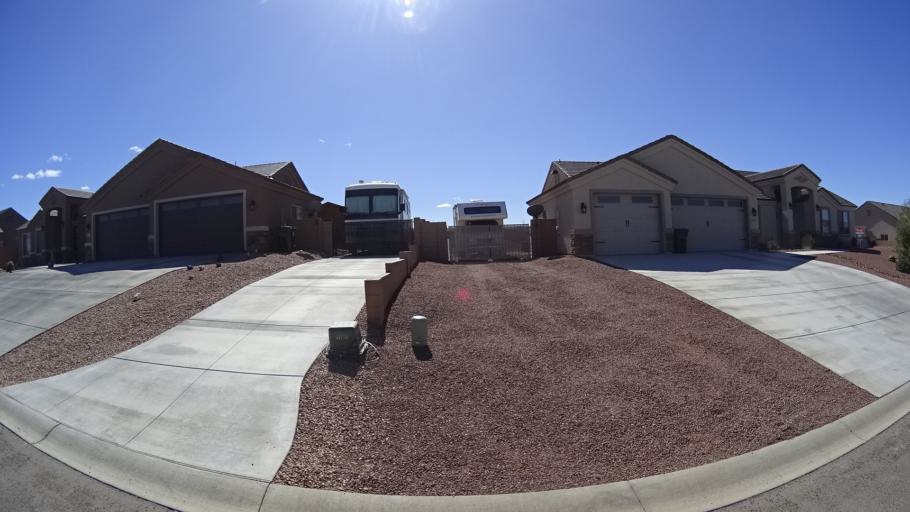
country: US
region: Arizona
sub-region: Mohave County
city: Kingman
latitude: 35.1965
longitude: -113.9670
